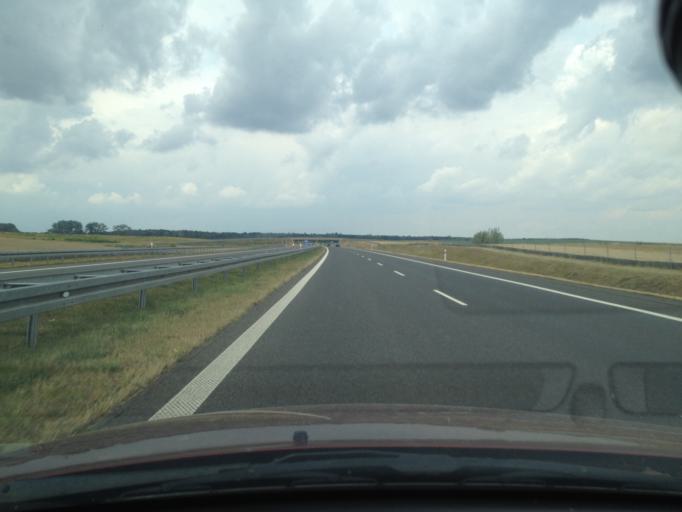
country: PL
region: West Pomeranian Voivodeship
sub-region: Powiat mysliborski
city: Mysliborz
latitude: 52.9825
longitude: 14.8882
